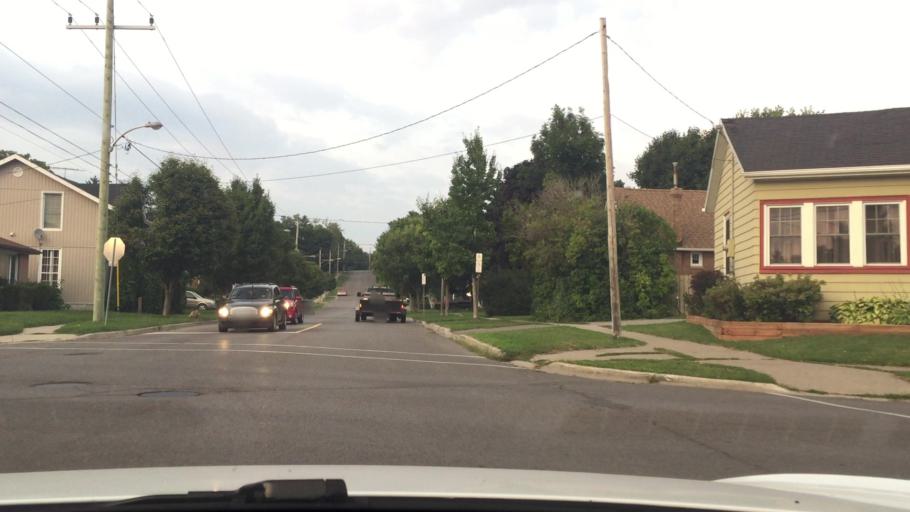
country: CA
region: Ontario
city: Cobourg
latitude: 43.9558
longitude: -78.2886
